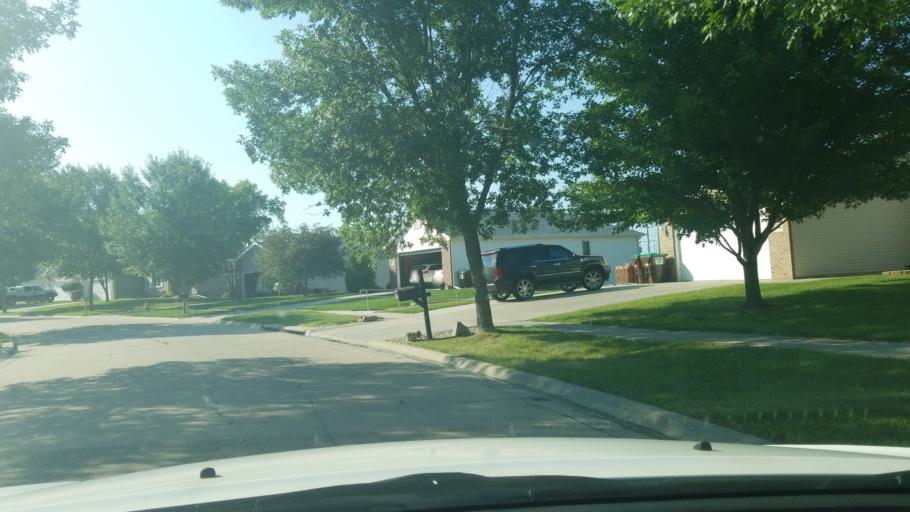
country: US
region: Nebraska
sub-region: Lancaster County
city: Lincoln
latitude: 40.7532
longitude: -96.6110
